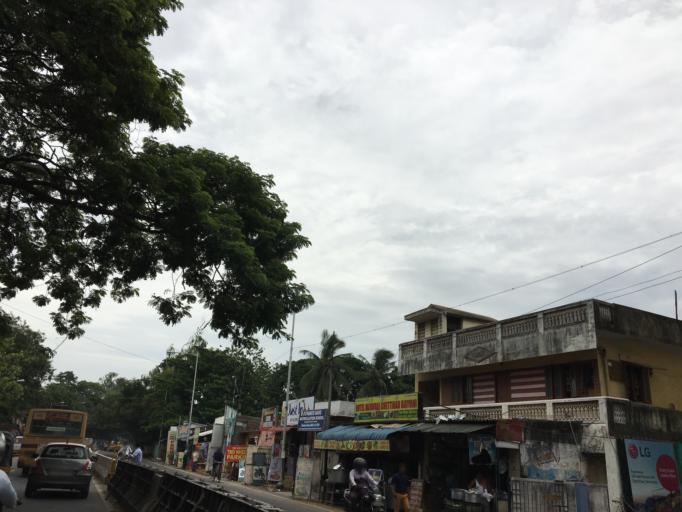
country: IN
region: Tamil Nadu
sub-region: Kancheepuram
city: Alandur
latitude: 12.9944
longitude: 80.2176
